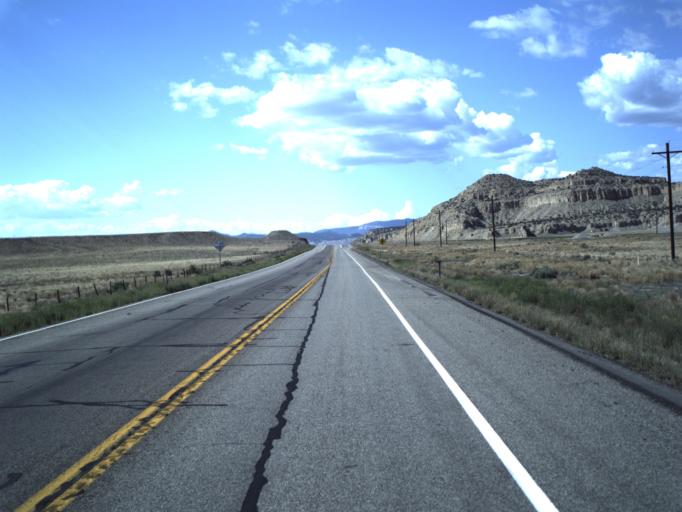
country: US
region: Utah
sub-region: Emery County
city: Ferron
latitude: 38.8557
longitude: -111.3048
